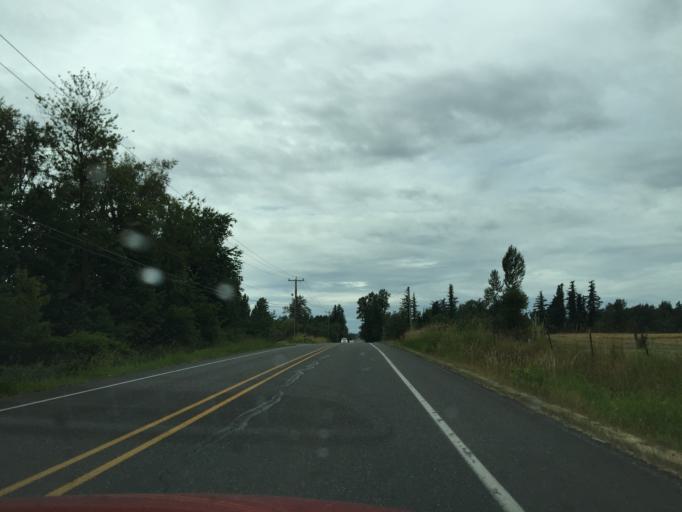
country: US
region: Washington
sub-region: Whatcom County
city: Everson
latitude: 48.9418
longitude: -122.3626
